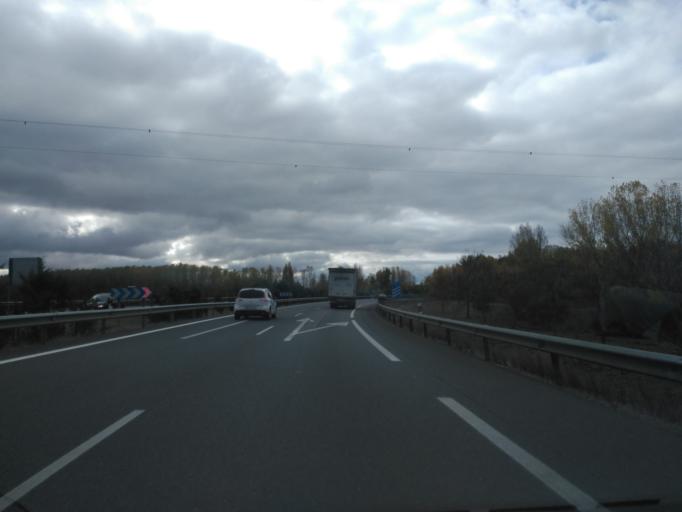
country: ES
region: Castille and Leon
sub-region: Provincia de Palencia
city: Duenas
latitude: 41.8923
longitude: -4.5248
